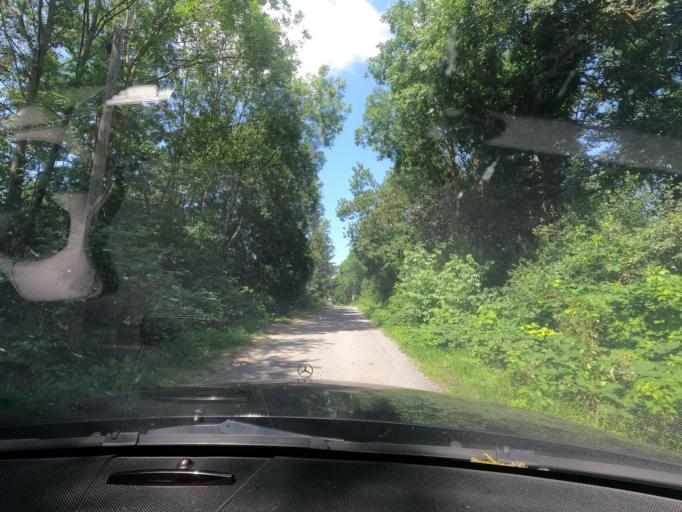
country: DE
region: Thuringia
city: Muehlhausen
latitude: 51.2109
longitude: 10.4251
